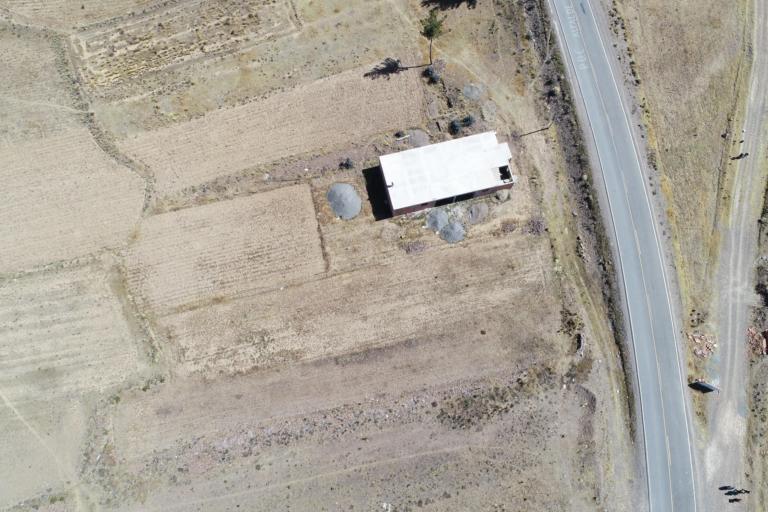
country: BO
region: La Paz
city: Achacachi
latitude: -15.9001
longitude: -68.9016
